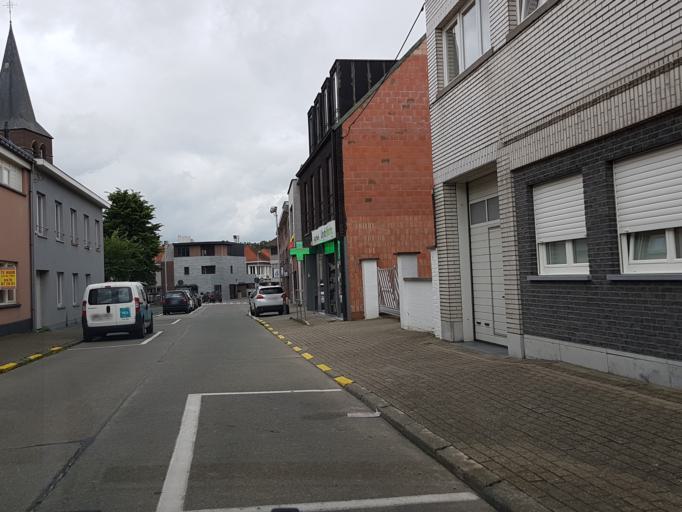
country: BE
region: Flanders
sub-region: Provincie Oost-Vlaanderen
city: Denderleeuw
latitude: 50.8925
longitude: 4.1003
